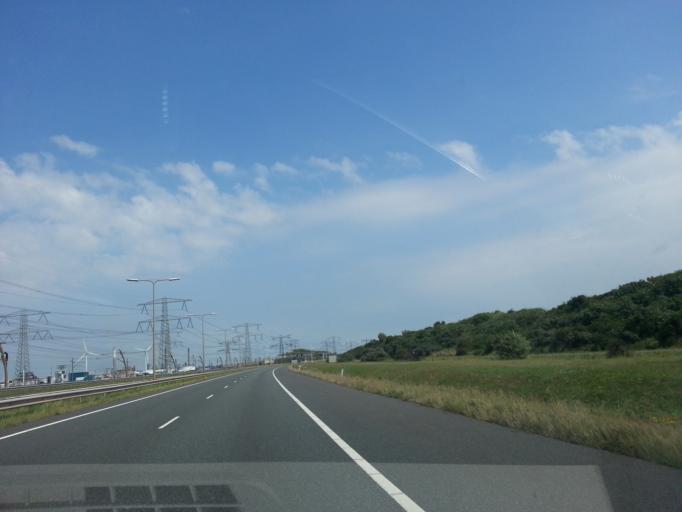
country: NL
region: South Holland
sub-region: Gemeente Rotterdam
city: Hoek van Holland
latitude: 51.9333
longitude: 4.0688
